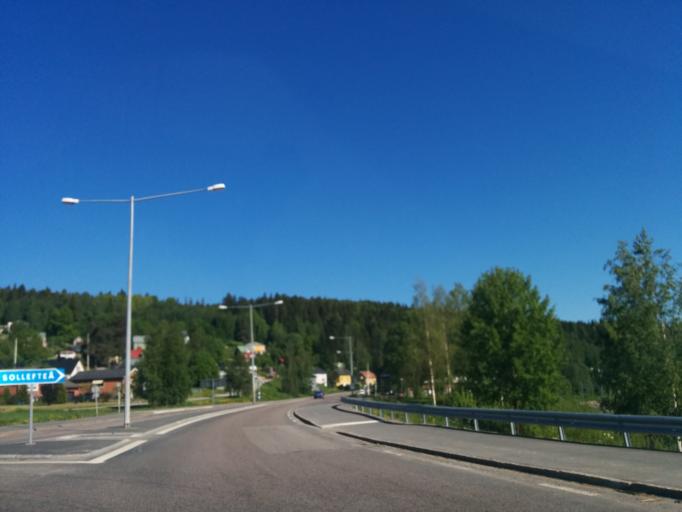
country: SE
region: Vaesternorrland
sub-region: Kramfors Kommun
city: Kramfors
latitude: 62.9347
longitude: 17.7716
